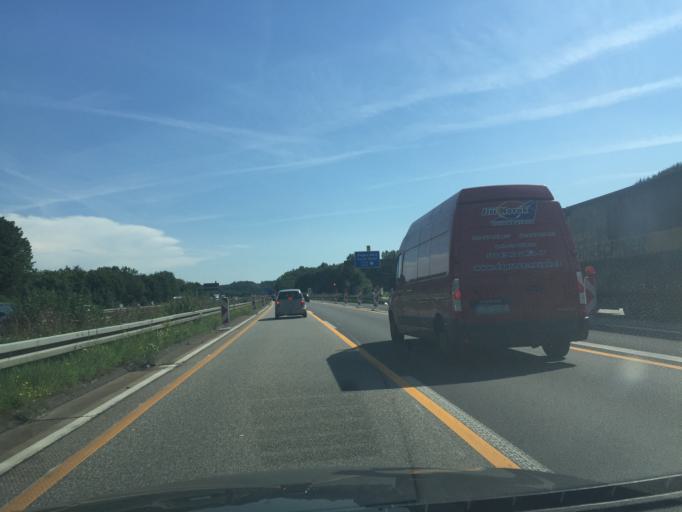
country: DE
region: North Rhine-Westphalia
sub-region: Regierungsbezirk Arnsberg
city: Olpe
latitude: 50.9920
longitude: 7.8345
